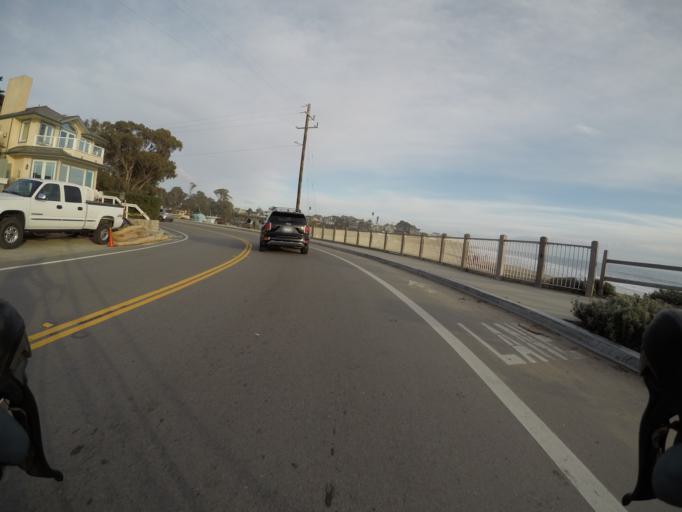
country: US
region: California
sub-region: Santa Cruz County
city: Twin Lakes
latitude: 36.9625
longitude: -121.9991
